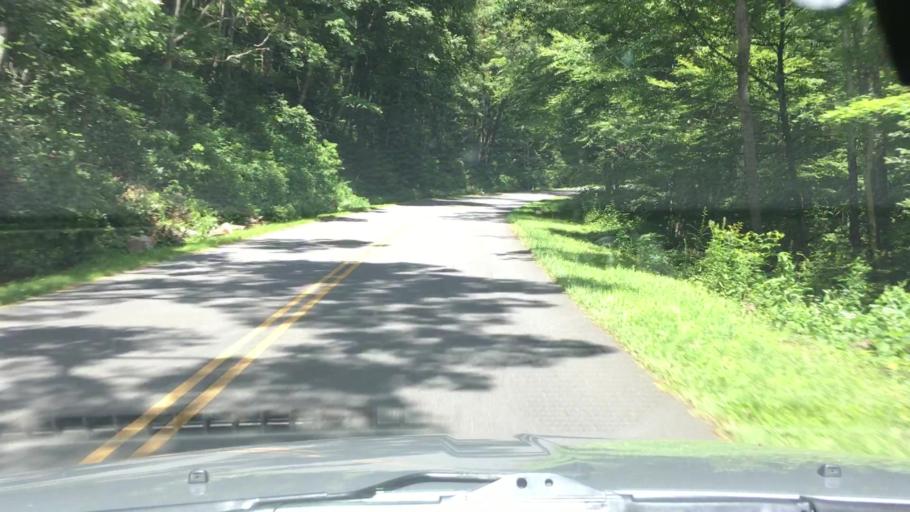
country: US
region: North Carolina
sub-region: Buncombe County
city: Swannanoa
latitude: 35.6667
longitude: -82.4480
